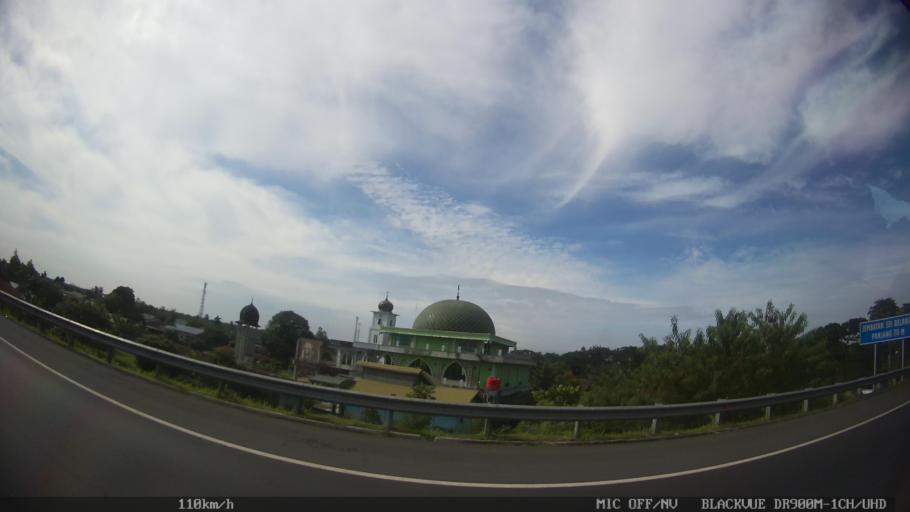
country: ID
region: North Sumatra
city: Sunggal
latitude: 3.6381
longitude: 98.5956
